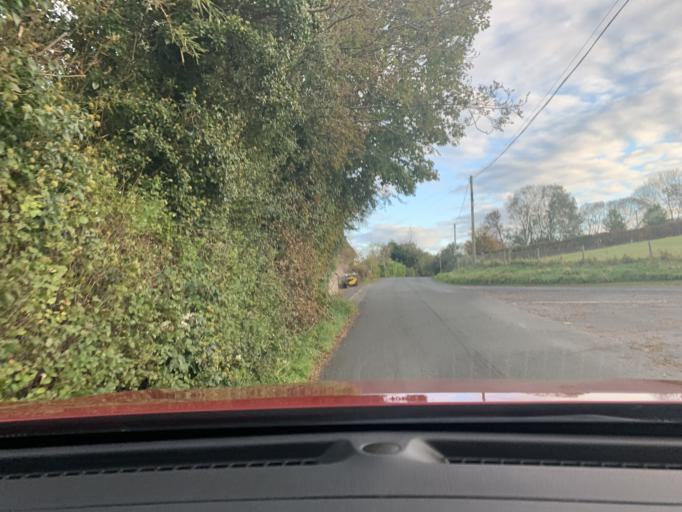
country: IE
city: Ballisodare
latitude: 54.2346
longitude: -8.5177
